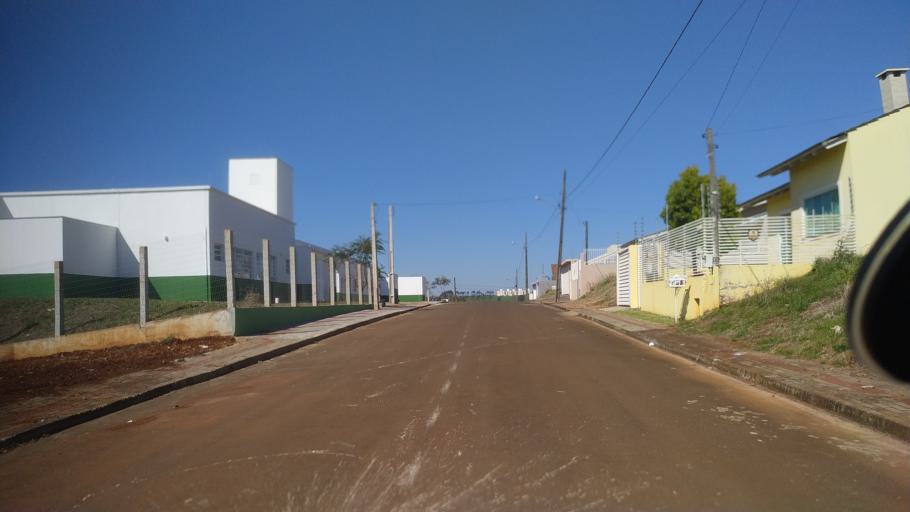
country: BR
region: Santa Catarina
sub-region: Chapeco
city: Chapeco
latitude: -27.0895
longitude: -52.5839
